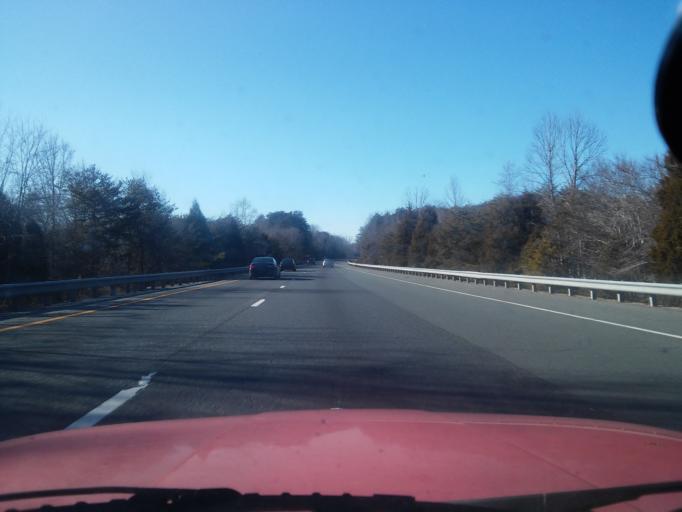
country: US
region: Virginia
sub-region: Fluvanna County
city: Lake Monticello
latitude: 37.9988
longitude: -78.3433
